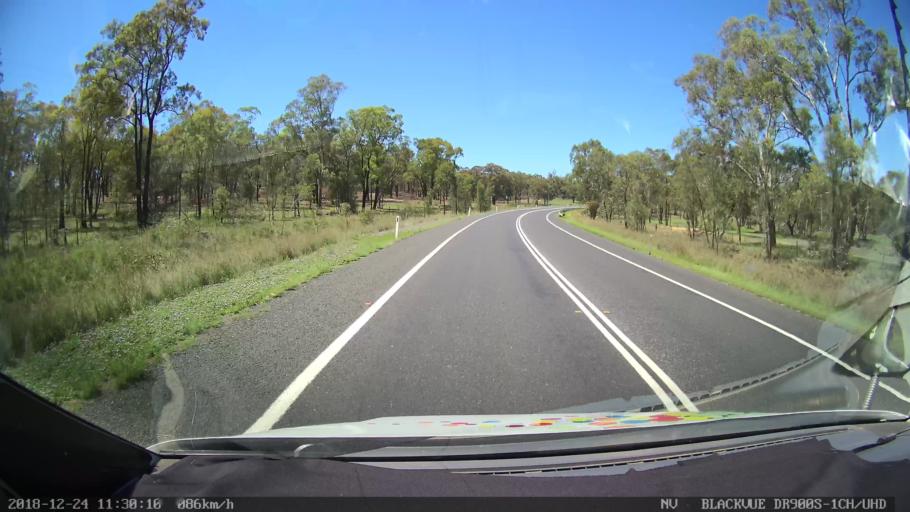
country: AU
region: New South Wales
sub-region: Upper Hunter Shire
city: Merriwa
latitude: -32.2014
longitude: 150.4674
